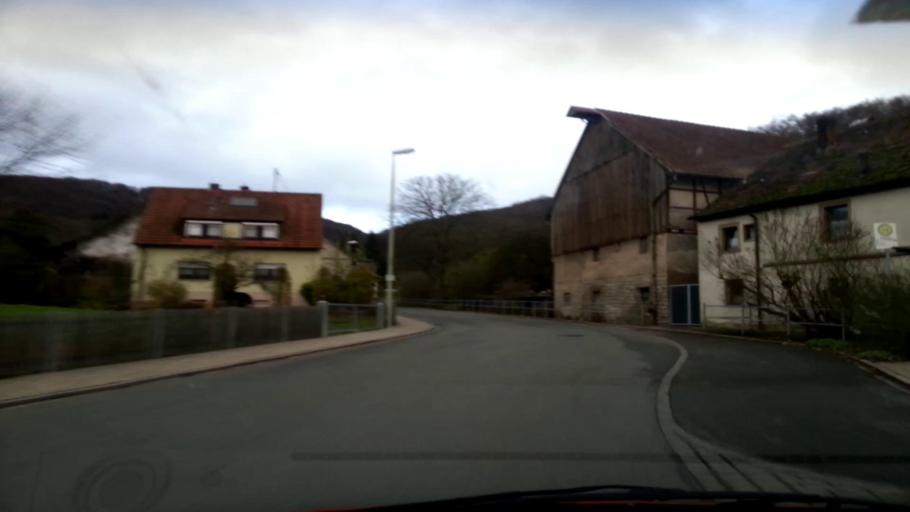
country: DE
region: Bavaria
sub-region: Upper Franconia
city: Poxdorf
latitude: 49.9184
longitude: 11.0748
